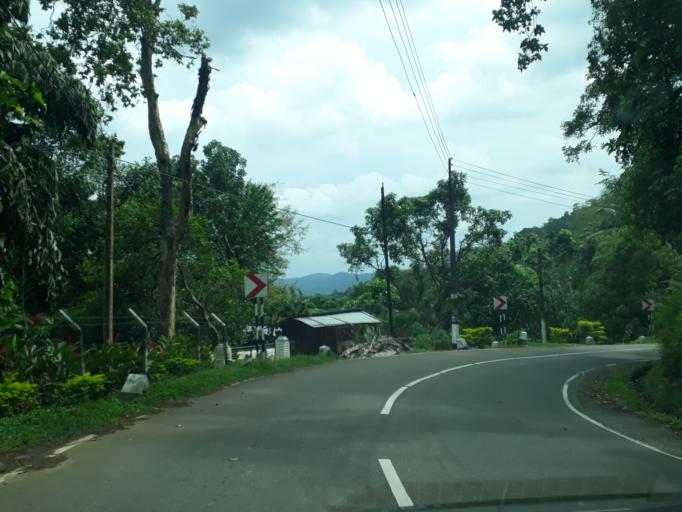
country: LK
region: Southern
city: Weligama
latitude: 6.3165
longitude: 80.5439
